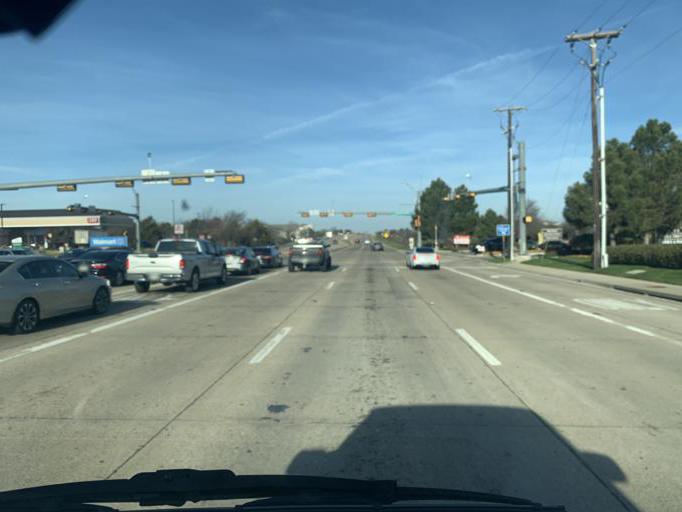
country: US
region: Texas
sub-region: Dallas County
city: Cedar Hill
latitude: 32.6003
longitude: -96.9441
